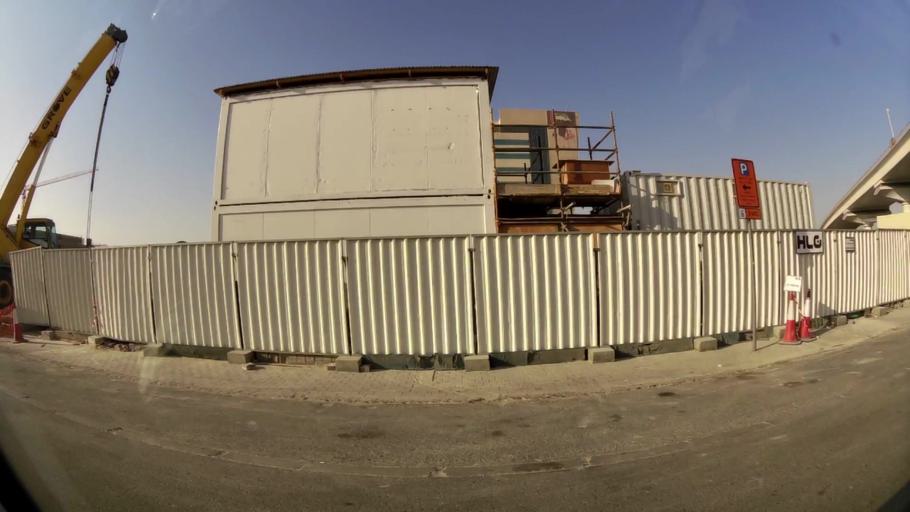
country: AE
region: Ash Shariqah
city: Sharjah
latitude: 25.2501
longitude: 55.3439
